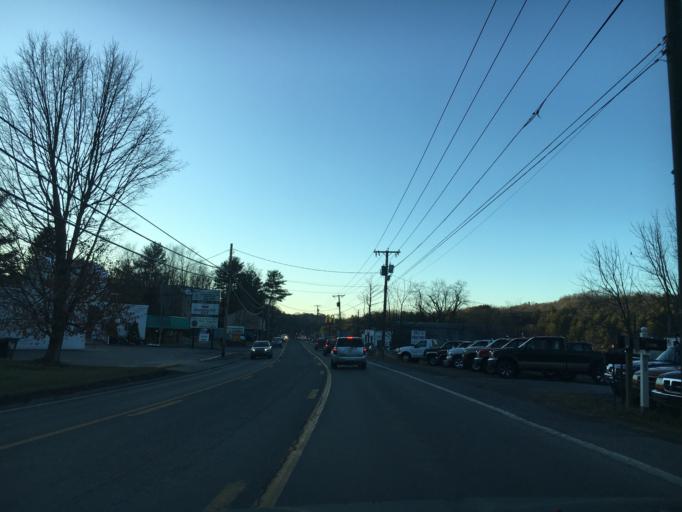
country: US
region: West Virginia
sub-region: Raleigh County
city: Daniels
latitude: 37.7484
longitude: -81.1312
